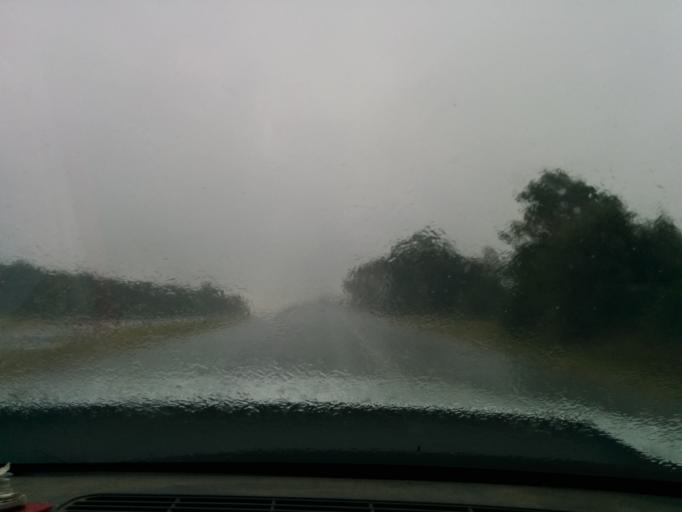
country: US
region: Oklahoma
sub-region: Okmulgee County
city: Beggs
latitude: 35.7345
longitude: -96.0047
